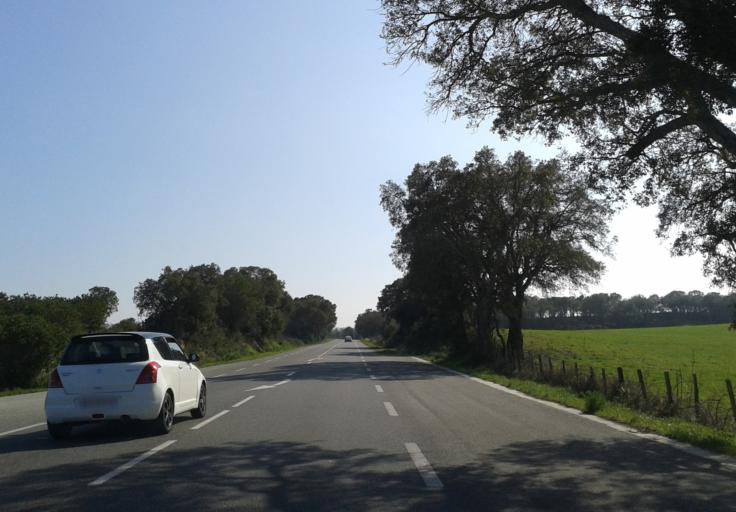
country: FR
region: Corsica
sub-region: Departement de la Haute-Corse
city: Linguizzetta
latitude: 42.2395
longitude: 9.5456
